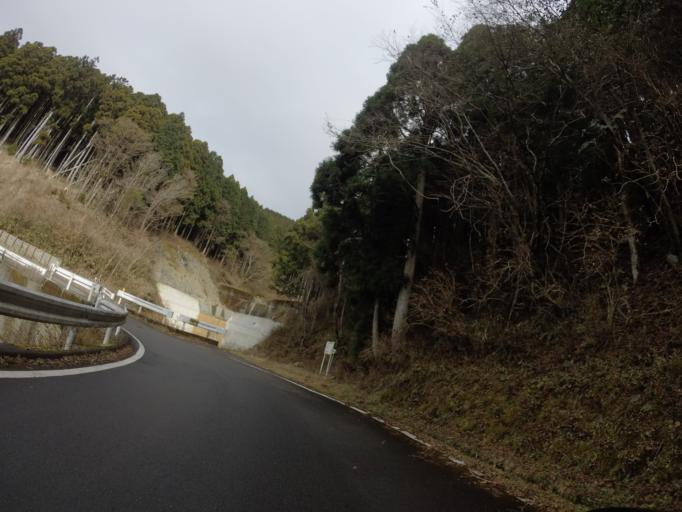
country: JP
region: Shizuoka
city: Heda
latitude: 34.8538
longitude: 138.8472
